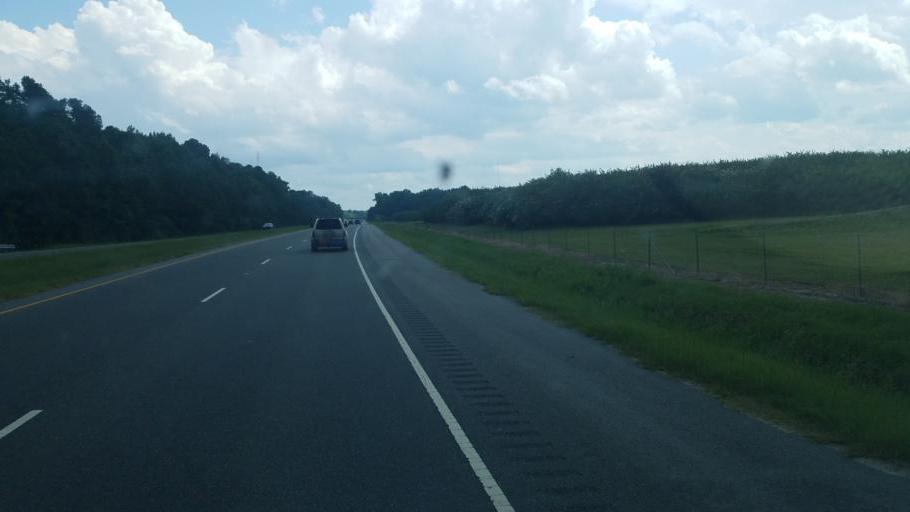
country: US
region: North Carolina
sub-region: Currituck County
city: Moyock
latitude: 36.6436
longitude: -76.2202
